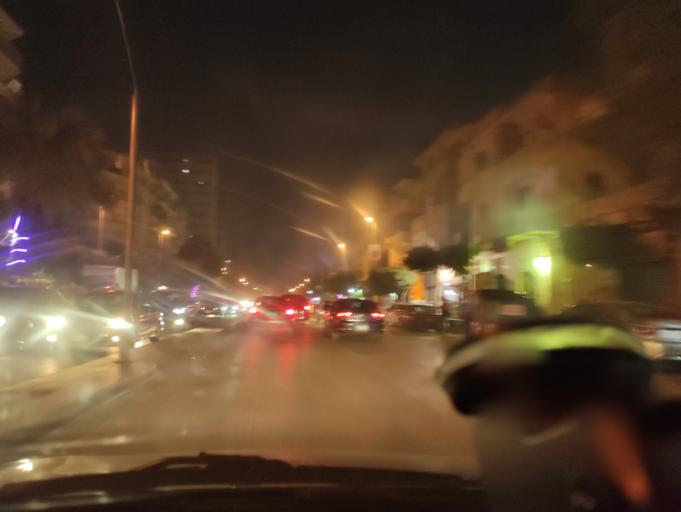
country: EG
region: Muhafazat al Qahirah
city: Cairo
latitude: 30.0916
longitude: 31.2800
